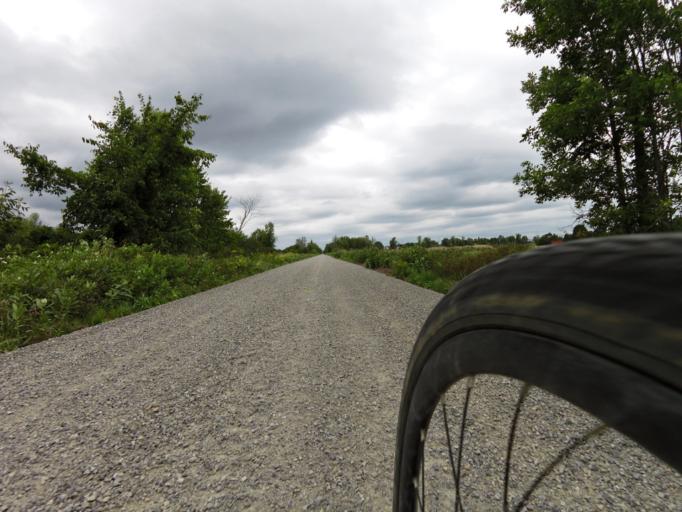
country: CA
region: Ontario
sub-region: Lanark County
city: Smiths Falls
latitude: 44.9252
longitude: -76.0316
